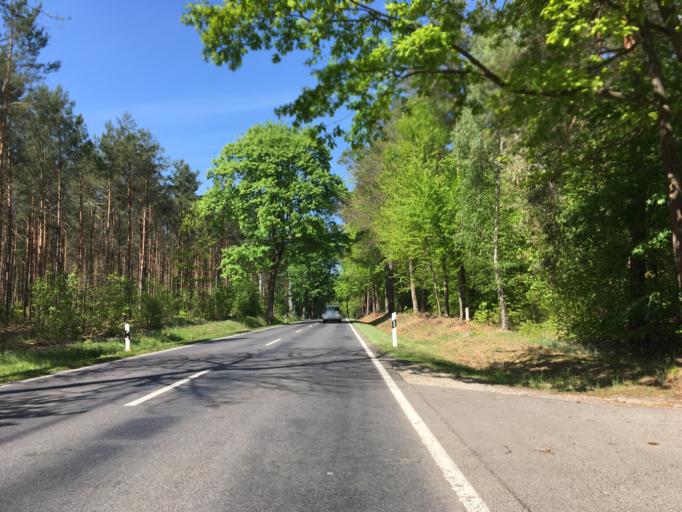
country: DE
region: Brandenburg
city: Marienwerder
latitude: 52.7794
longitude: 13.5584
